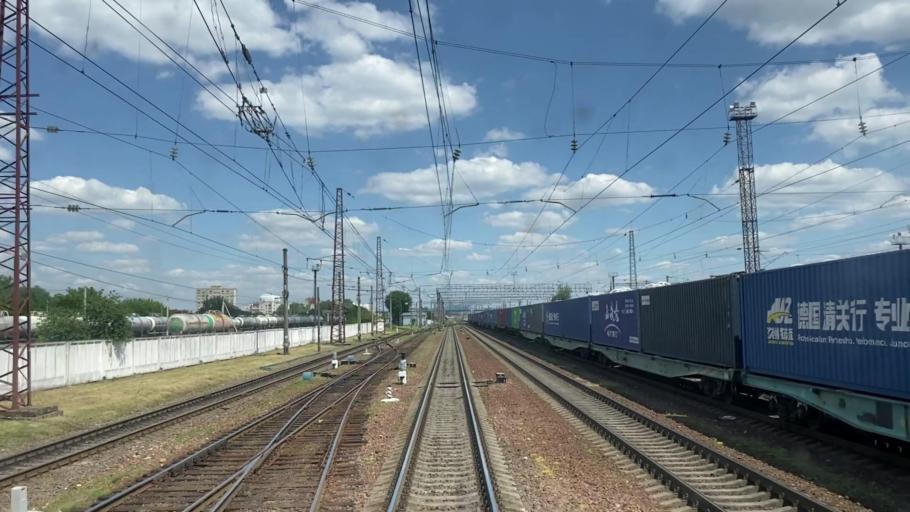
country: BY
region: Brest
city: Brest
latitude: 52.1091
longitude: 23.7188
